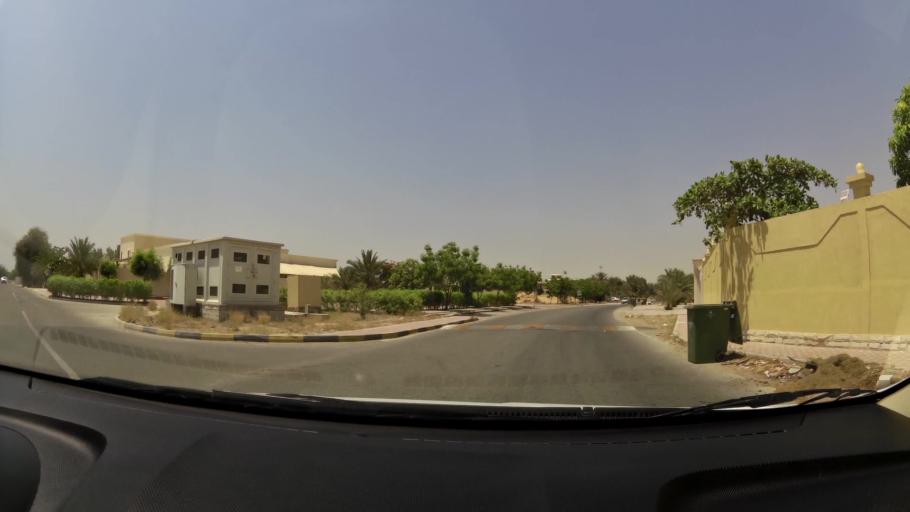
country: AE
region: Ajman
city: Ajman
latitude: 25.4191
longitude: 55.5059
